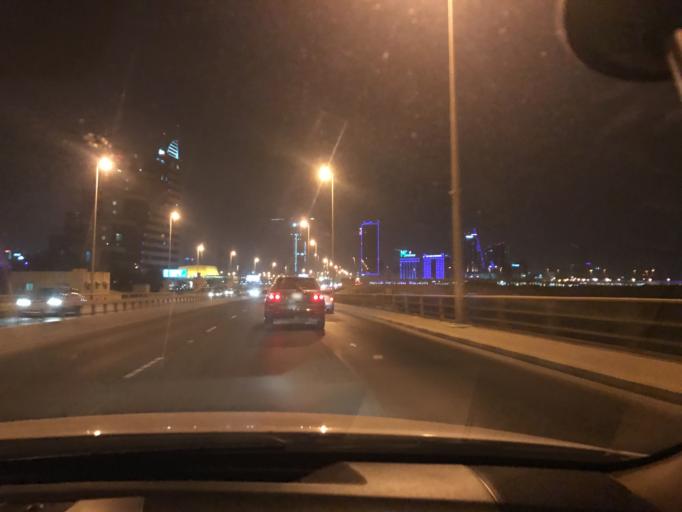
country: BH
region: Muharraq
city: Al Muharraq
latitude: 26.2482
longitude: 50.6036
